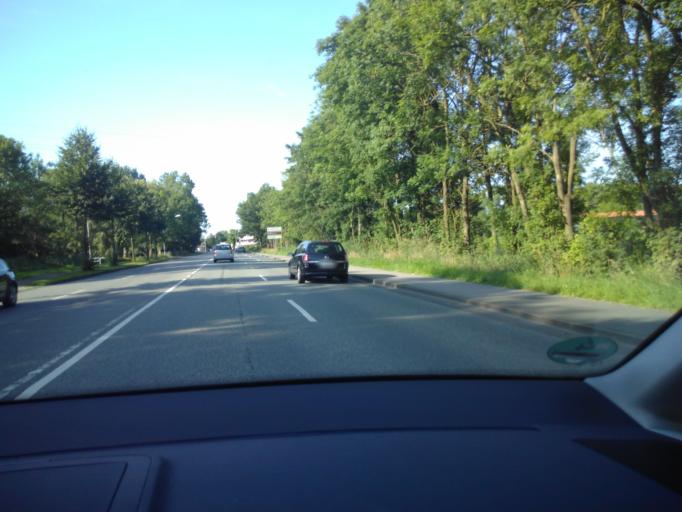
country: DE
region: Lower Saxony
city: Cuxhaven
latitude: 53.8413
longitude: 8.6839
